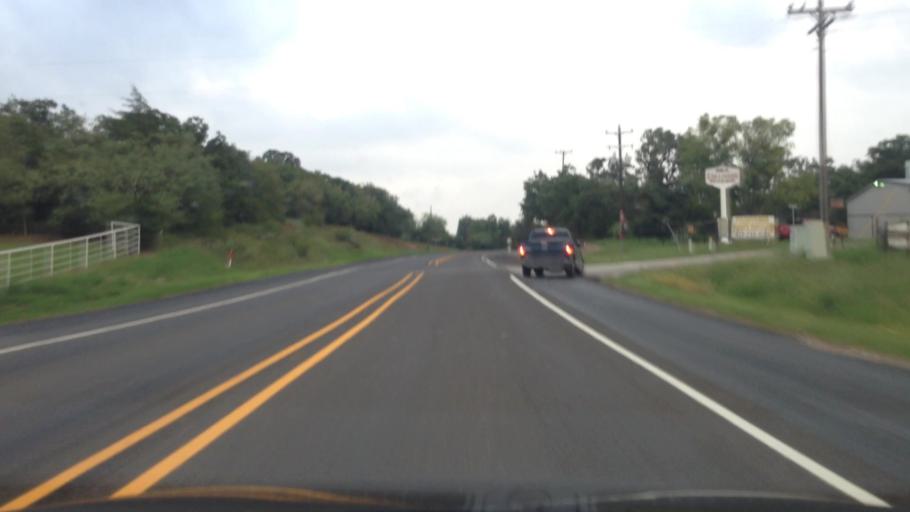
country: US
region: Texas
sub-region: Johnson County
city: Burleson
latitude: 32.4983
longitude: -97.3382
